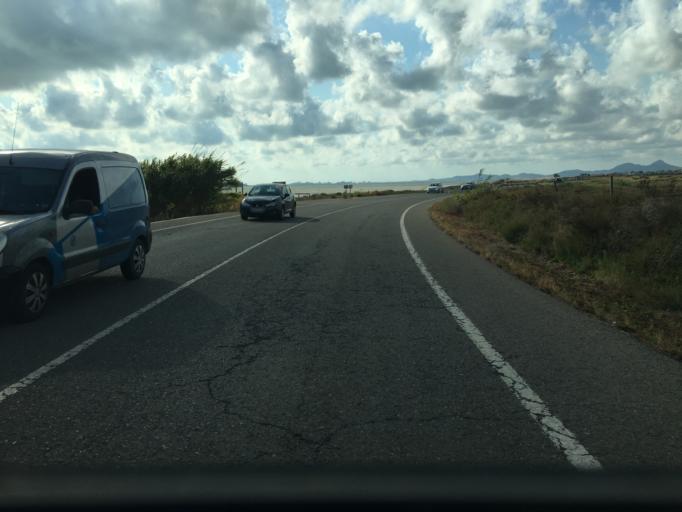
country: ES
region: Murcia
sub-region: Murcia
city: Los Alcazares
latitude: 37.7139
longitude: -0.8584
